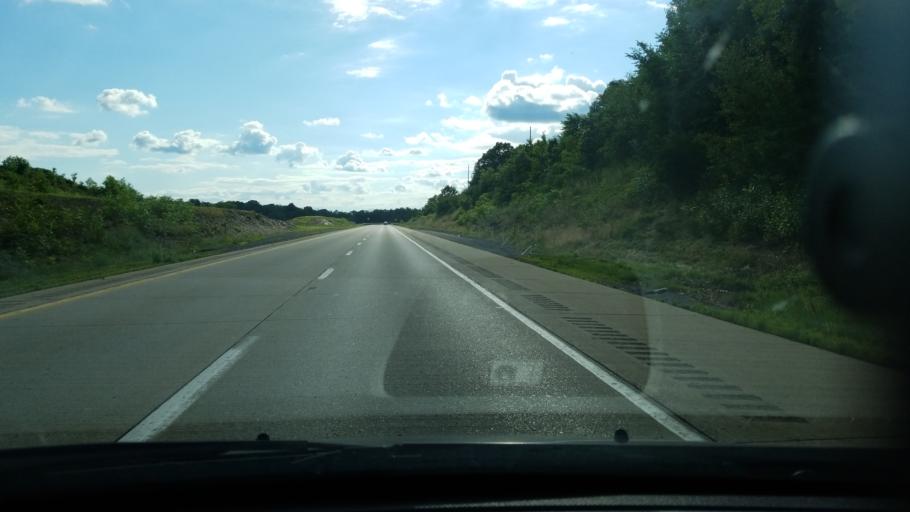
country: US
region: Pennsylvania
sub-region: Northumberland County
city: Riverside
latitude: 40.9869
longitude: -76.7089
